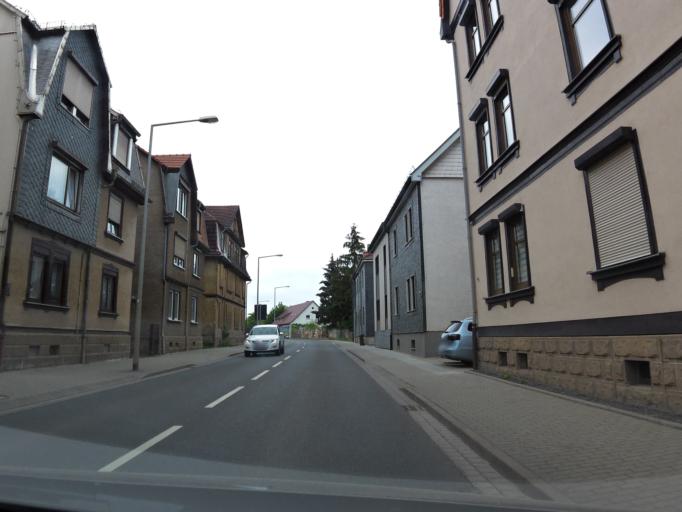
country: DE
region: Thuringia
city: Gotha
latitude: 50.9468
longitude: 10.7274
